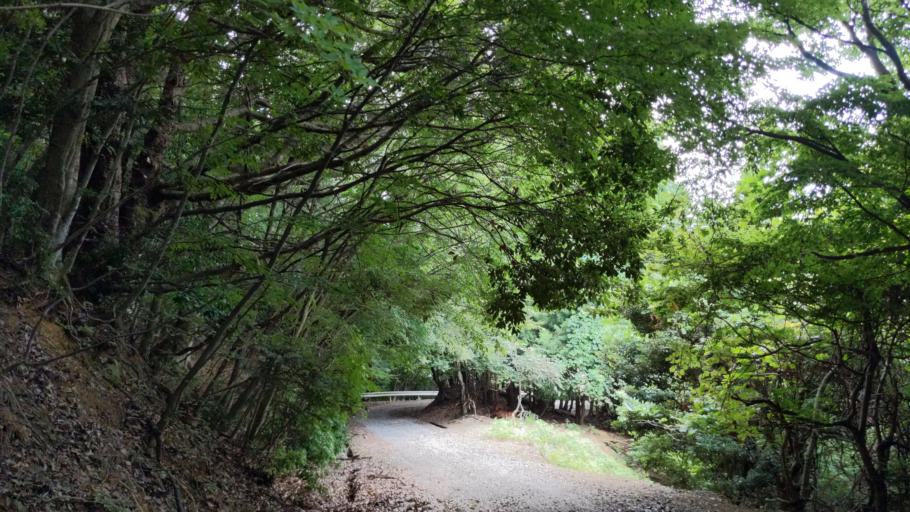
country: JP
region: Kyoto
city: Maizuru
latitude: 35.3900
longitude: 135.4382
